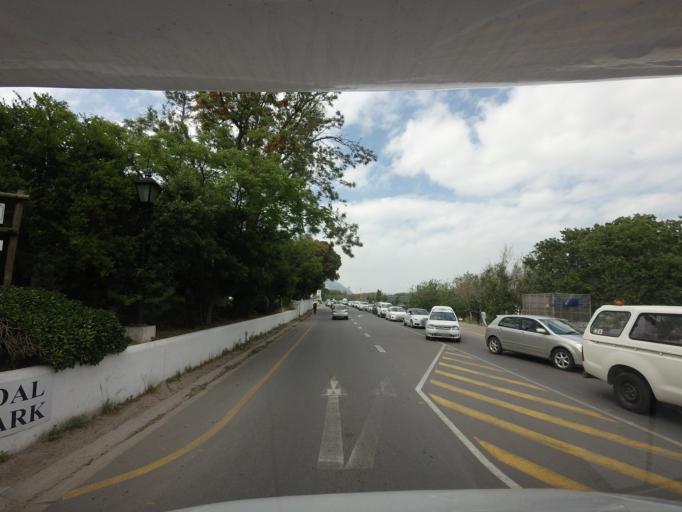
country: ZA
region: Western Cape
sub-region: City of Cape Town
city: Constantia
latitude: -34.0325
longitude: 18.3564
